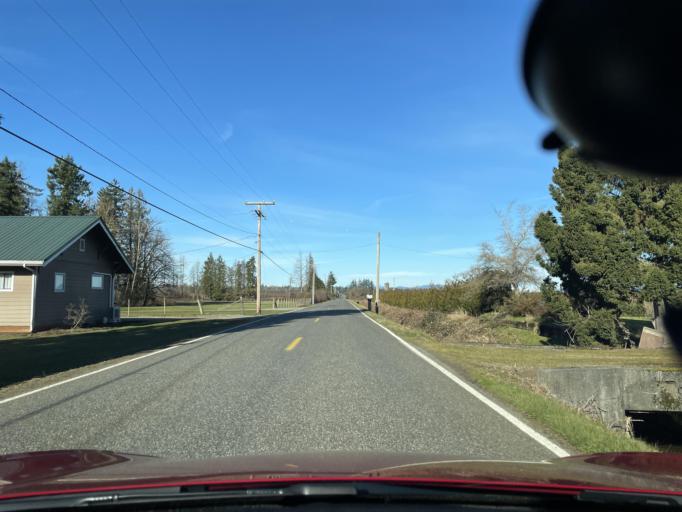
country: US
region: Washington
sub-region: Whatcom County
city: Lynden
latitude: 48.9590
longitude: -122.5303
